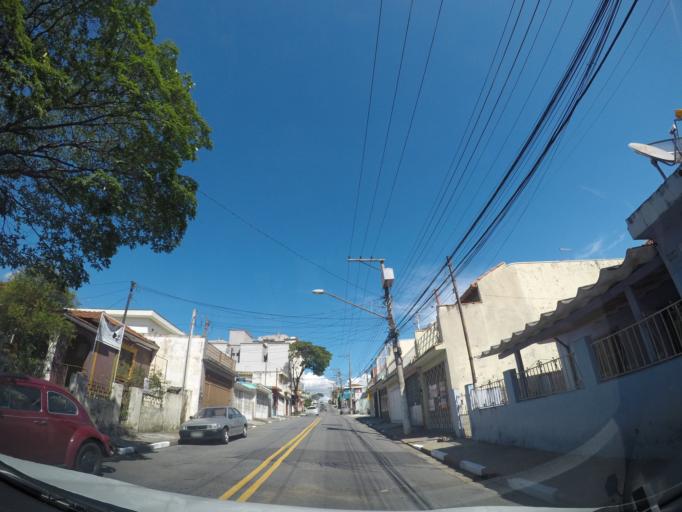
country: BR
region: Sao Paulo
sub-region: Guarulhos
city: Guarulhos
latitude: -23.4522
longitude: -46.5499
